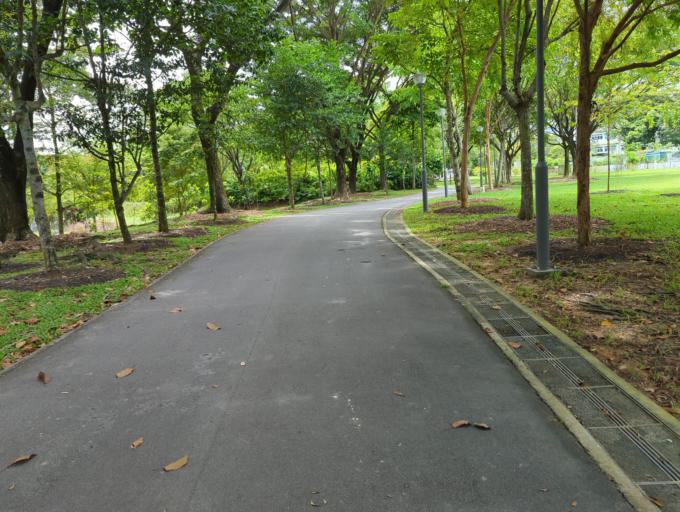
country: MY
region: Johor
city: Kampung Pasir Gudang Baru
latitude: 1.4118
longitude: 103.9020
